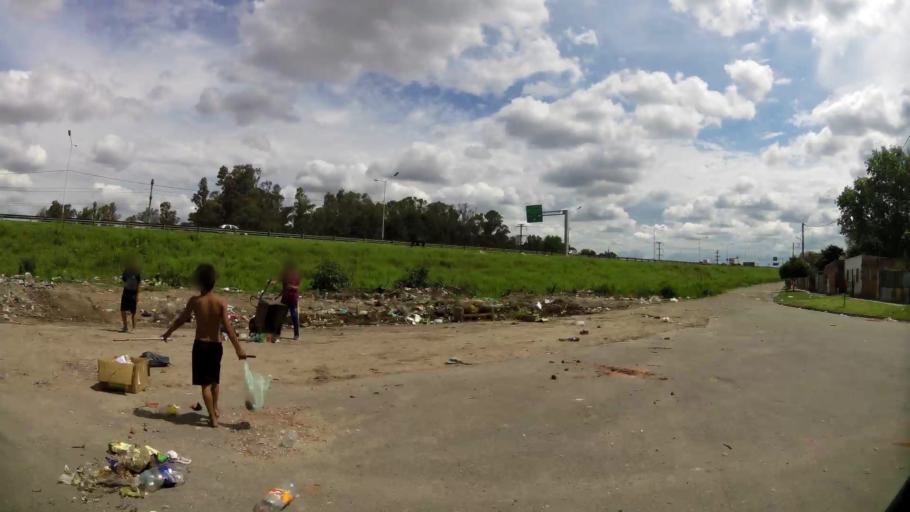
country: AR
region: Santa Fe
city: Gobernador Galvez
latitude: -33.0156
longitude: -60.6412
